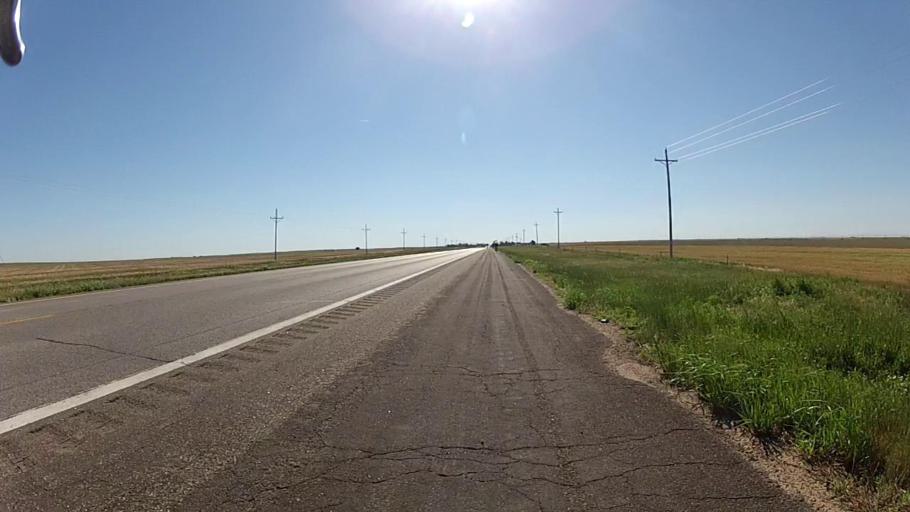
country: US
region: Kansas
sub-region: Kiowa County
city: Greensburg
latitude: 37.5863
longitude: -99.6111
